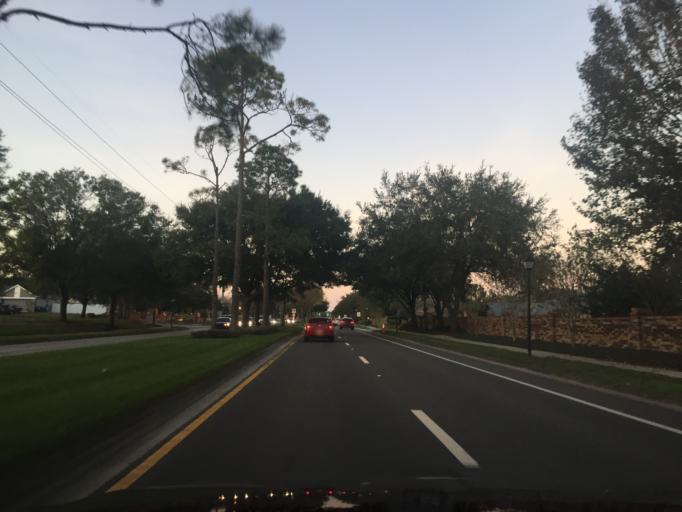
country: US
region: Florida
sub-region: Seminole County
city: Oviedo
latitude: 28.6523
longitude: -81.1792
